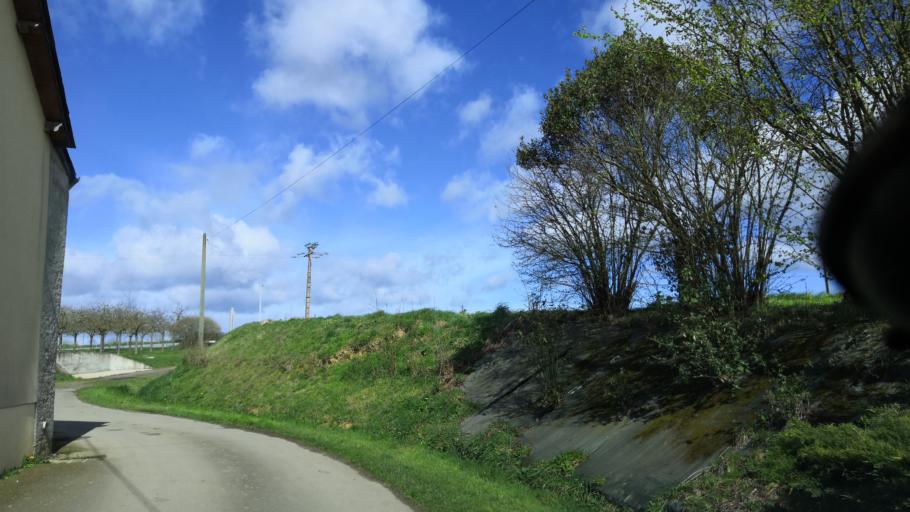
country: FR
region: Brittany
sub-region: Departement d'Ille-et-Vilaine
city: Bedee
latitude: 48.1860
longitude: -1.9744
